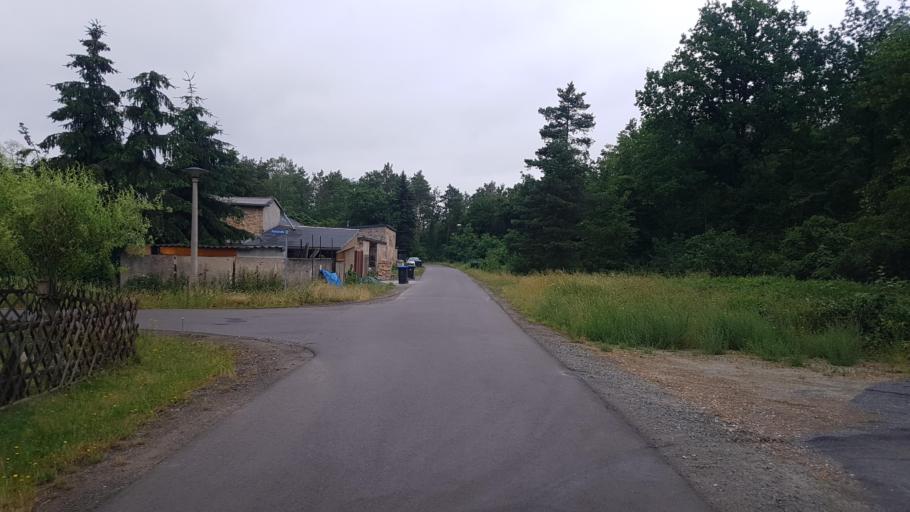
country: DE
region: Brandenburg
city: Schwarzbach
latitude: 51.4822
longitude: 13.9125
